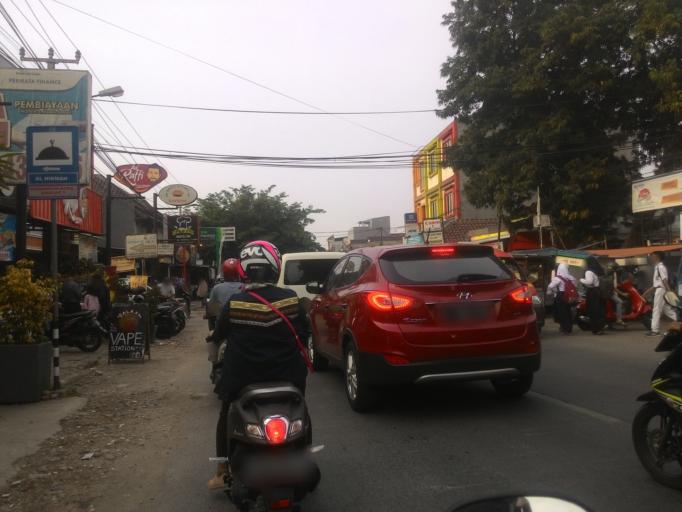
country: ID
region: West Java
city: Depok
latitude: -6.3959
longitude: 106.8366
